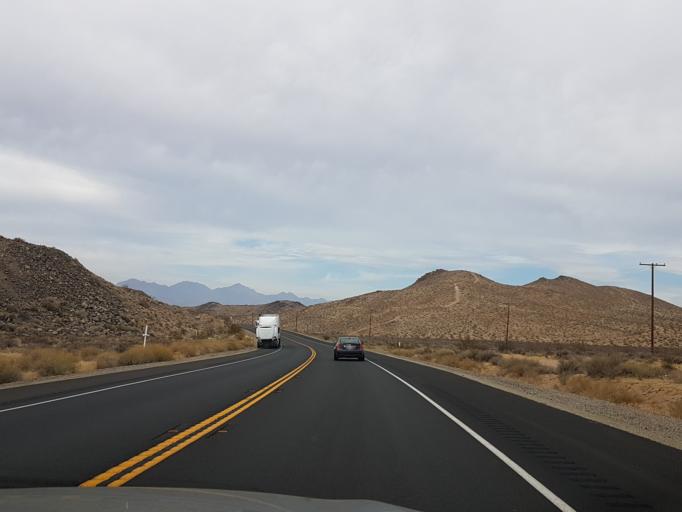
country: US
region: California
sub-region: Kern County
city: Ridgecrest
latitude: 35.5427
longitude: -117.6890
